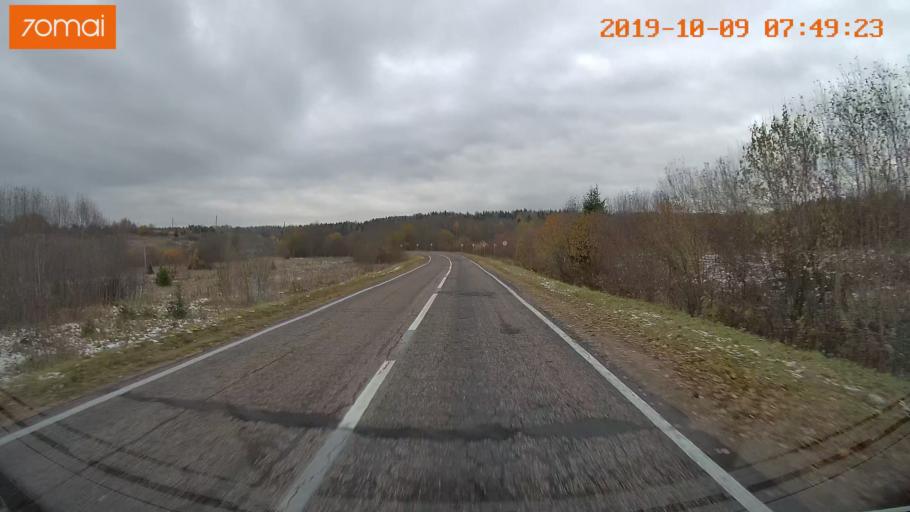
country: RU
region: Jaroslavl
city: Kukoboy
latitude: 58.6674
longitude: 39.8462
